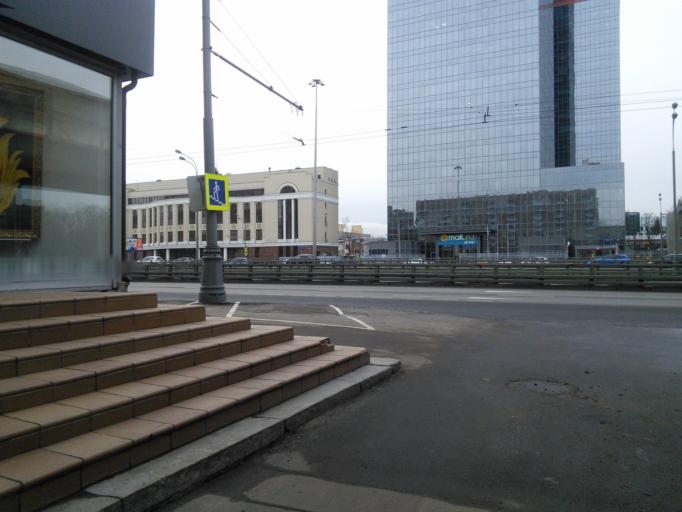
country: RU
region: Moscow
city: Sokol
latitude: 55.7982
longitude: 37.5389
